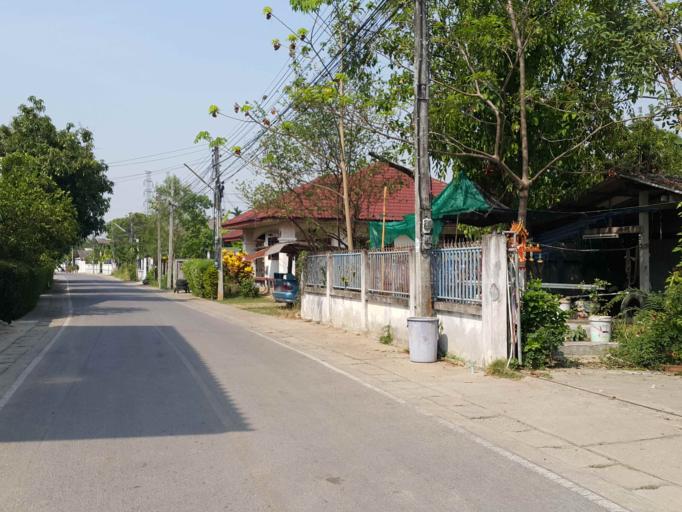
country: TH
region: Chiang Mai
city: San Kamphaeng
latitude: 18.7493
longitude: 99.0720
